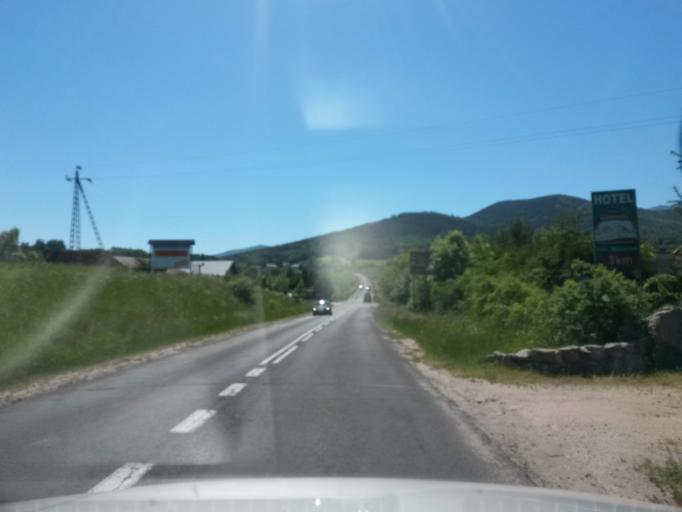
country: PL
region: Lower Silesian Voivodeship
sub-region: Powiat jeleniogorski
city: Sosnowka
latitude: 50.8266
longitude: 15.7237
